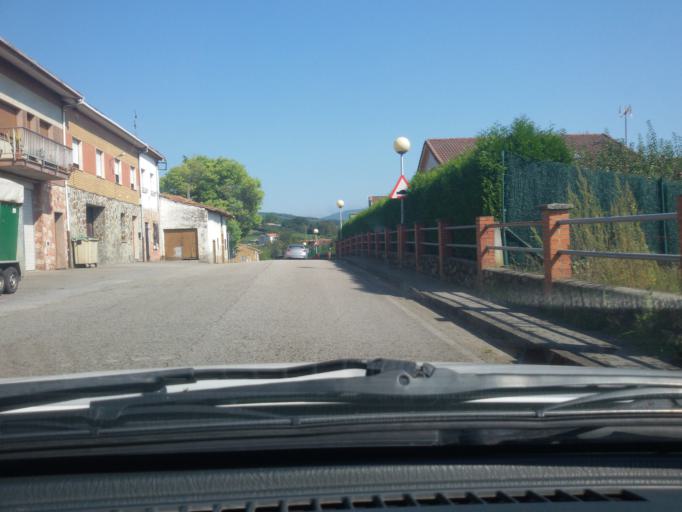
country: ES
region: Asturias
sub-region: Province of Asturias
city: Pola de Siero
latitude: 43.3904
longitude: -5.6726
